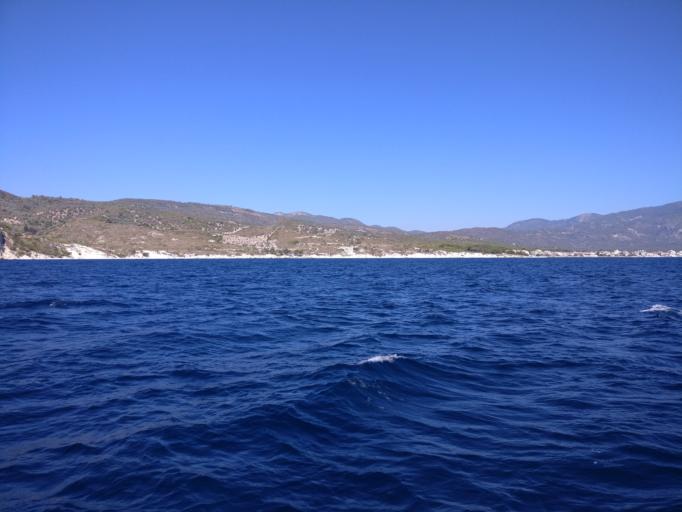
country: GR
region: North Aegean
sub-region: Nomos Samou
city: Chora
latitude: 37.6508
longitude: 26.8927
